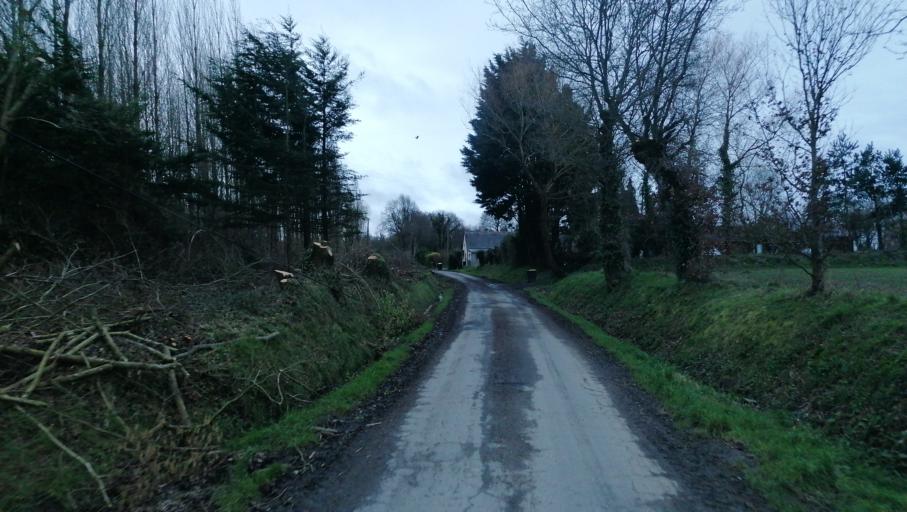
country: FR
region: Brittany
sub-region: Departement des Cotes-d'Armor
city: Goudelin
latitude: 48.5754
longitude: -3.0527
